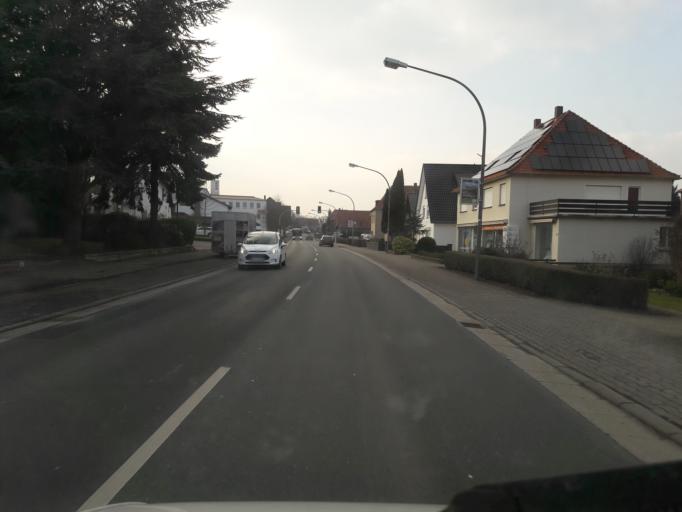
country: DE
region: North Rhine-Westphalia
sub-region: Regierungsbezirk Detmold
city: Huellhorst
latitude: 52.3008
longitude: 8.7030
